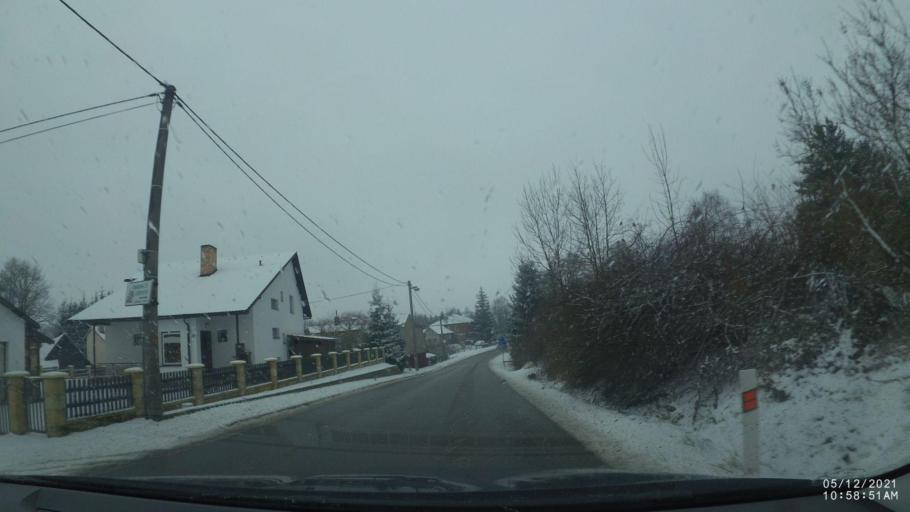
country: CZ
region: Kralovehradecky
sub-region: Okres Rychnov nad Kneznou
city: Rychnov nad Kneznou
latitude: 50.1633
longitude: 16.2419
